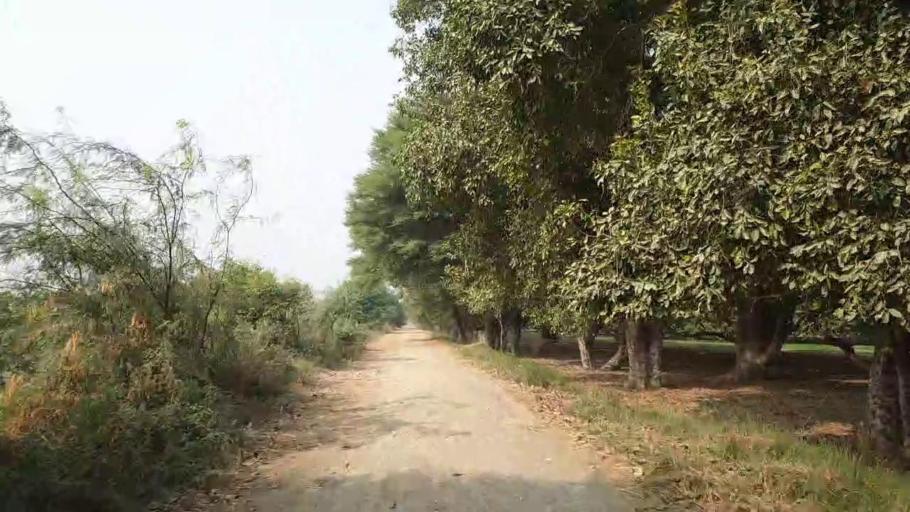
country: PK
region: Sindh
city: Tando Muhammad Khan
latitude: 25.2163
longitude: 68.5553
